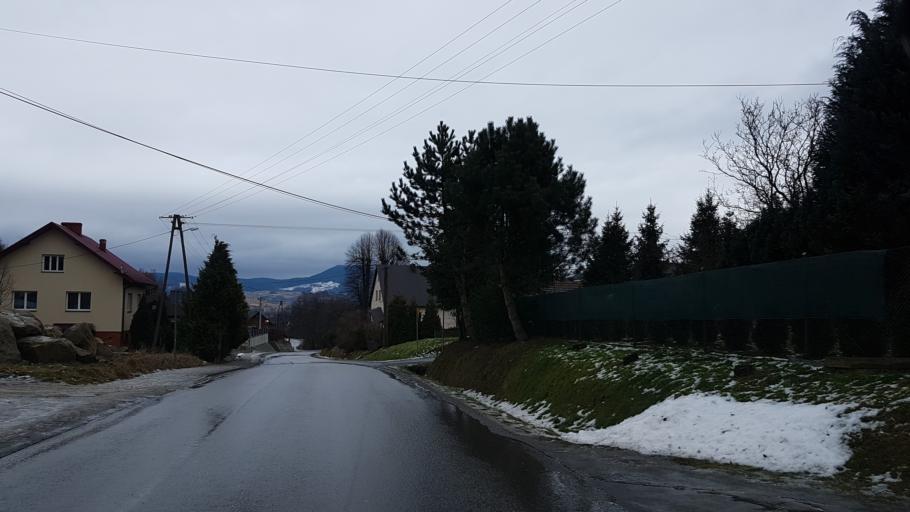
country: PL
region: Lesser Poland Voivodeship
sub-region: Powiat nowosadecki
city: Stary Sacz
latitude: 49.5119
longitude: 20.6036
